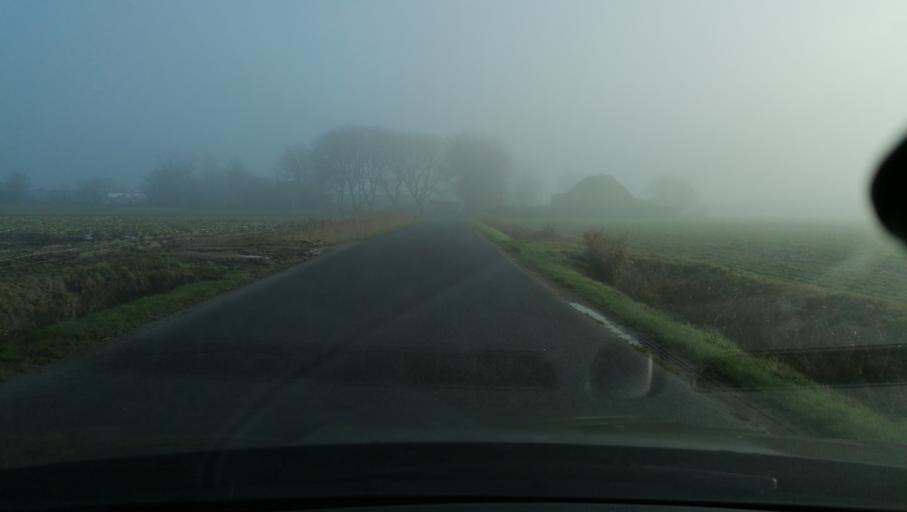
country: DE
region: Schleswig-Holstein
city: Meldorf
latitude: 54.0981
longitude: 9.0573
